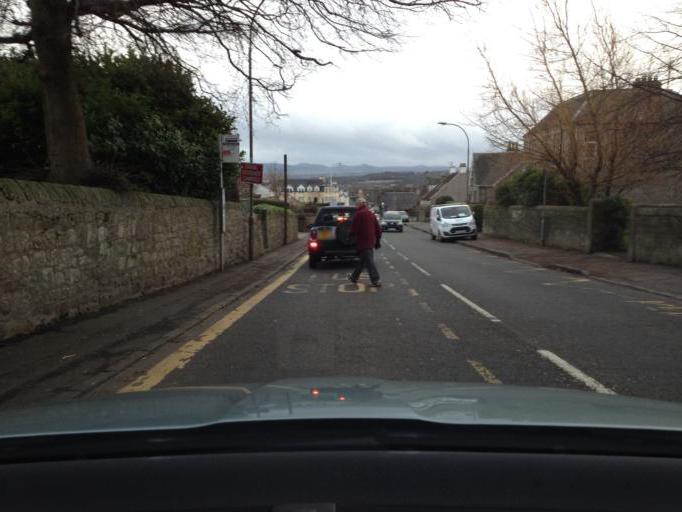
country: GB
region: Scotland
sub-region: Edinburgh
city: Kirkliston
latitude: 55.9578
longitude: -3.4031
